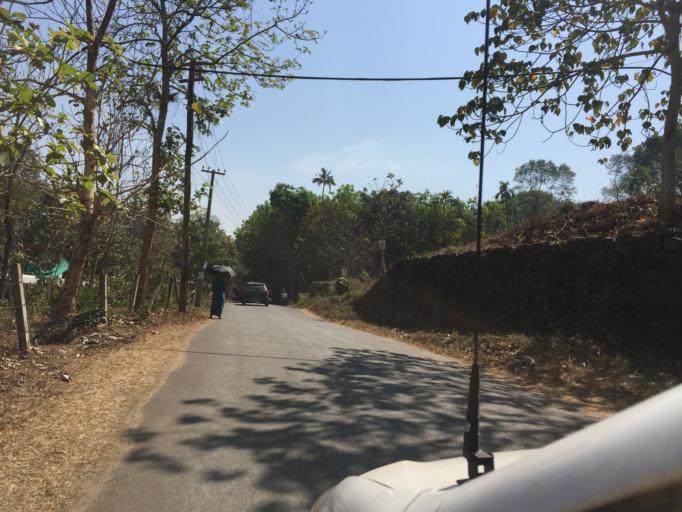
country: IN
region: Kerala
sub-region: Kottayam
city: Erattupetta
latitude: 9.6870
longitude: 76.7639
